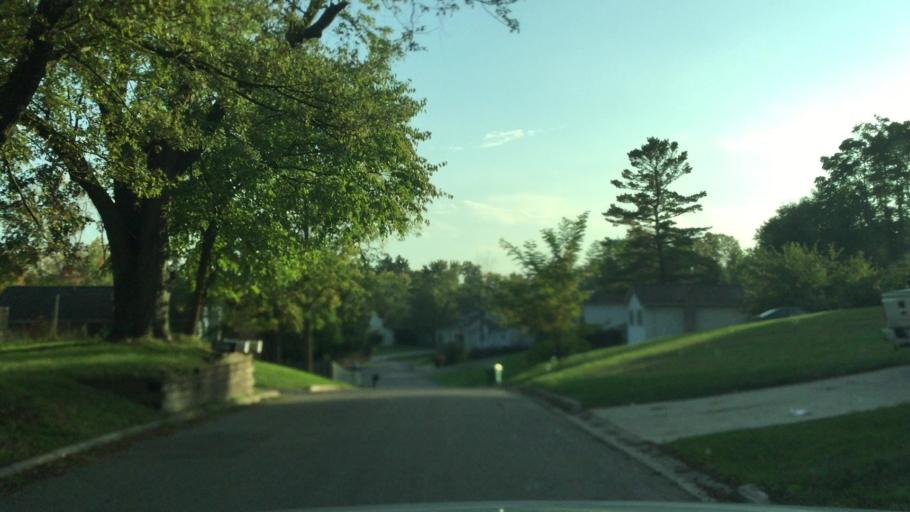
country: US
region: Michigan
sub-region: Oakland County
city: Keego Harbor
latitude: 42.6266
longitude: -83.3867
